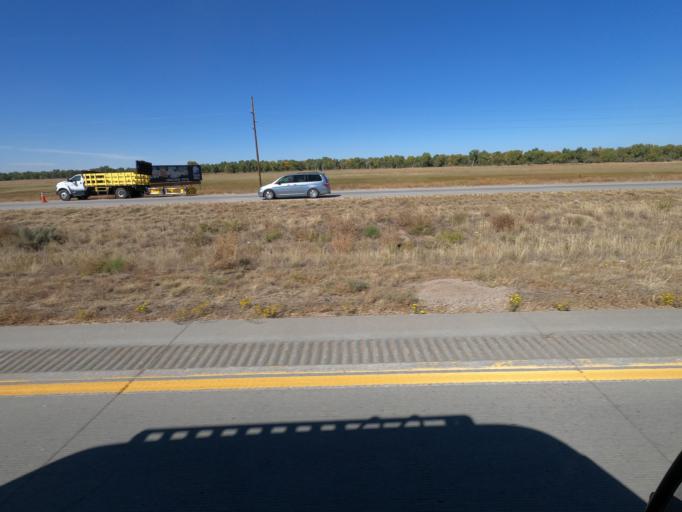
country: US
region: Colorado
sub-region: Morgan County
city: Fort Morgan
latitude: 40.2642
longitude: -103.7458
